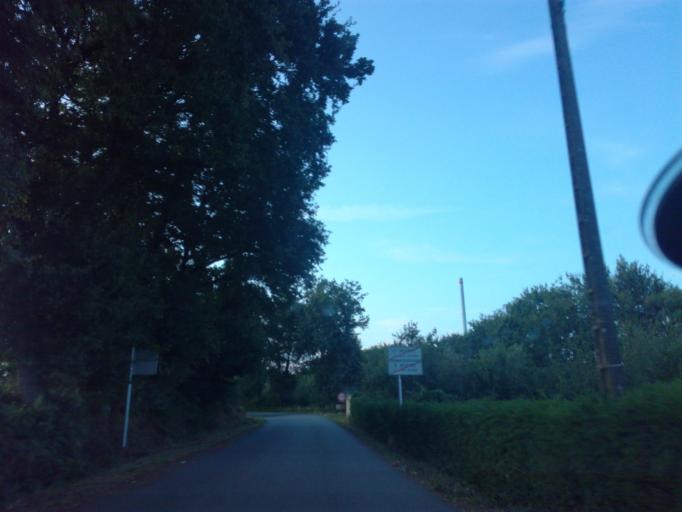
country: FR
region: Brittany
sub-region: Departement du Morbihan
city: Le Sourn
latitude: 48.0493
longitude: -2.9655
